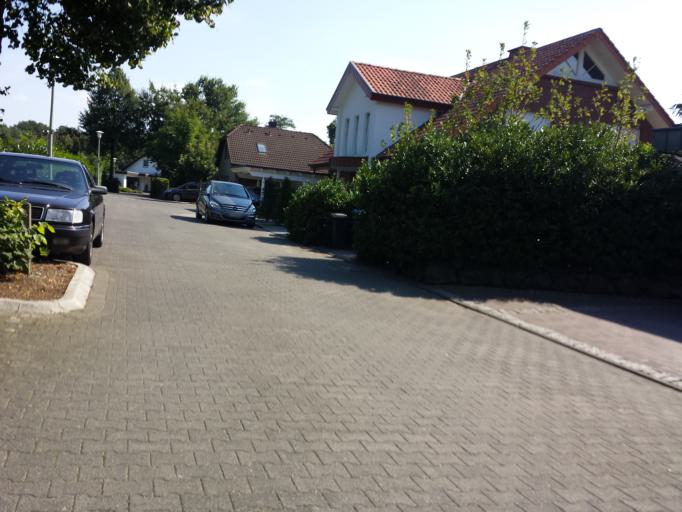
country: DE
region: North Rhine-Westphalia
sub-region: Regierungsbezirk Detmold
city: Guetersloh
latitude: 51.8784
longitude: 8.3786
